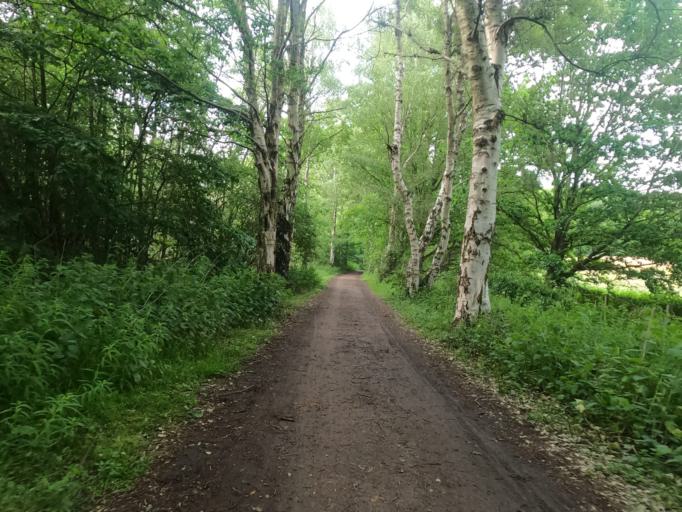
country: GB
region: England
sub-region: Cheshire West and Chester
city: Cuddington
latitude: 53.2258
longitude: -2.6195
